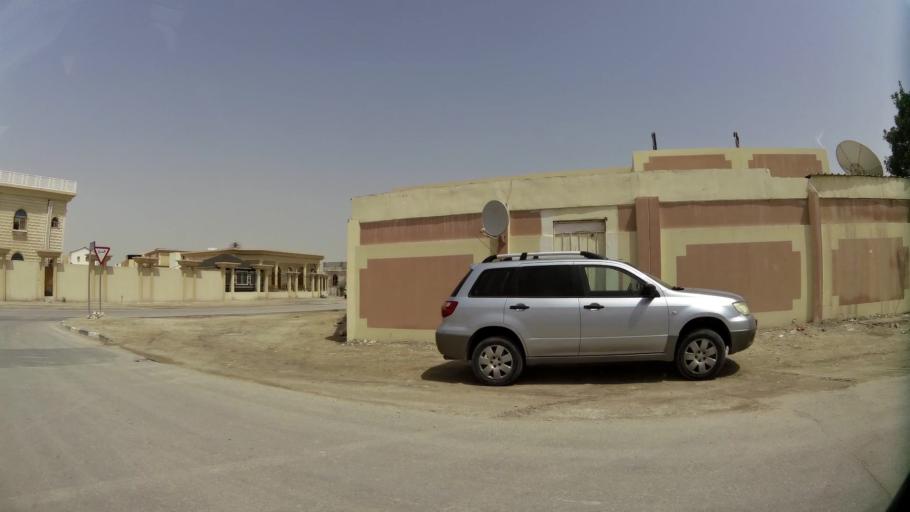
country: QA
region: Baladiyat ar Rayyan
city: Ar Rayyan
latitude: 25.2326
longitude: 51.4177
